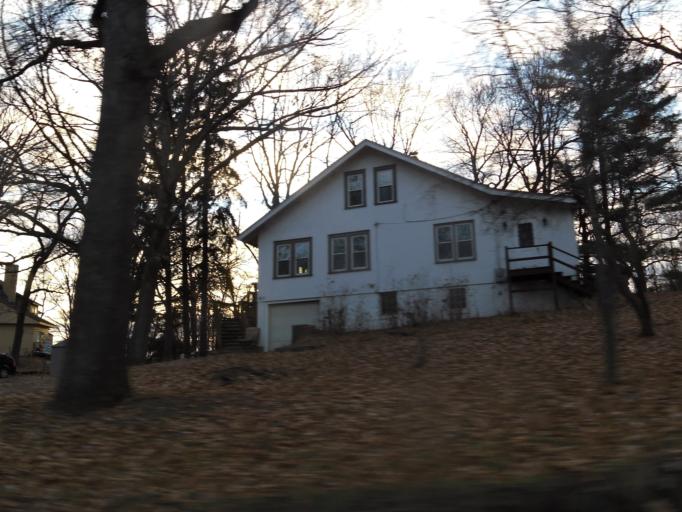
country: US
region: Minnesota
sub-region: Washington County
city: Mahtomedi
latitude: 45.0766
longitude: -92.9616
